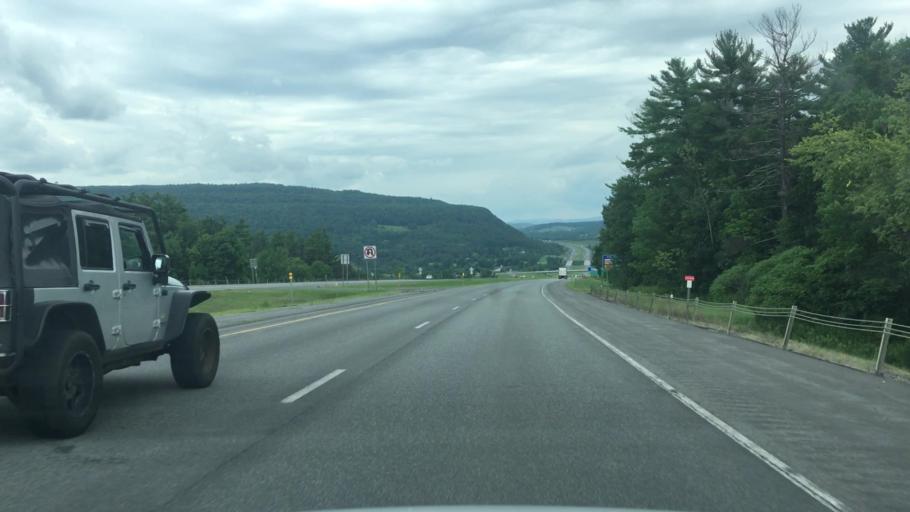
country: US
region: New York
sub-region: Schoharie County
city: Schoharie
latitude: 42.7097
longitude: -74.3004
